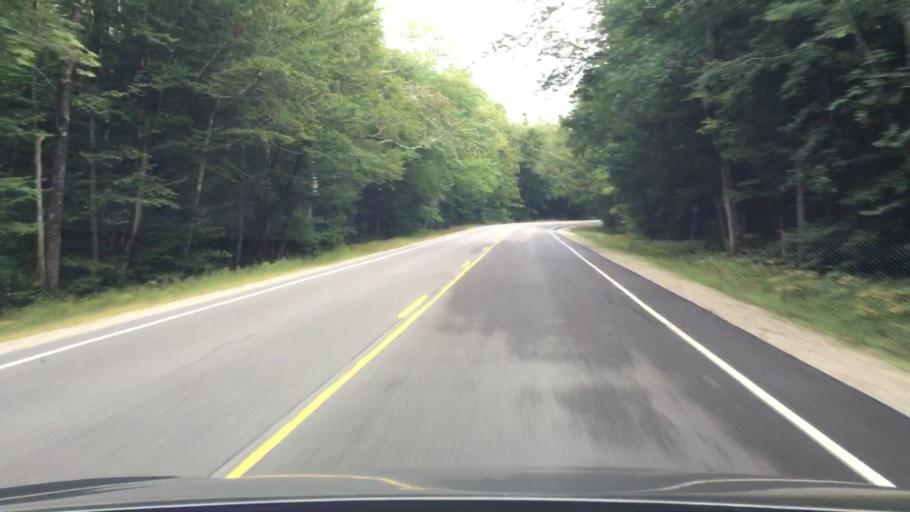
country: US
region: New Hampshire
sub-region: Carroll County
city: Tamworth
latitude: 43.9974
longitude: -71.3849
